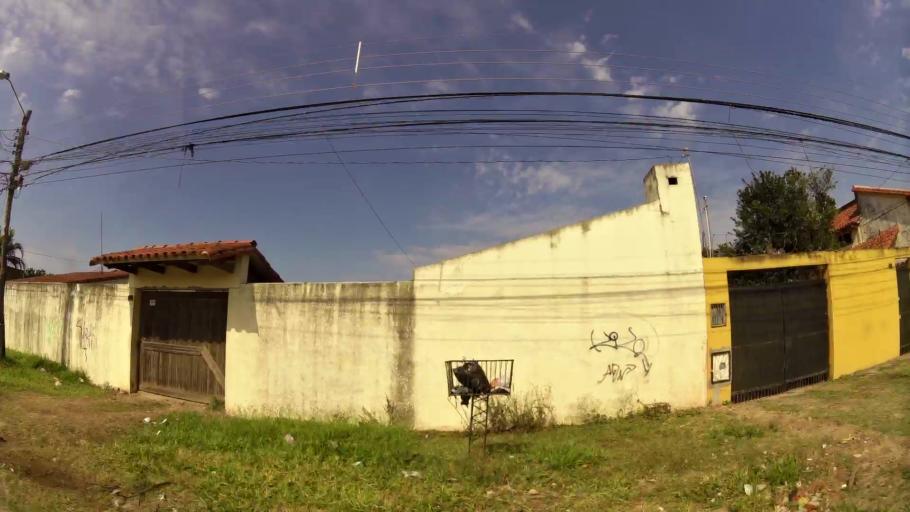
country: BO
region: Santa Cruz
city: Santa Cruz de la Sierra
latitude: -17.7311
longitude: -63.1440
